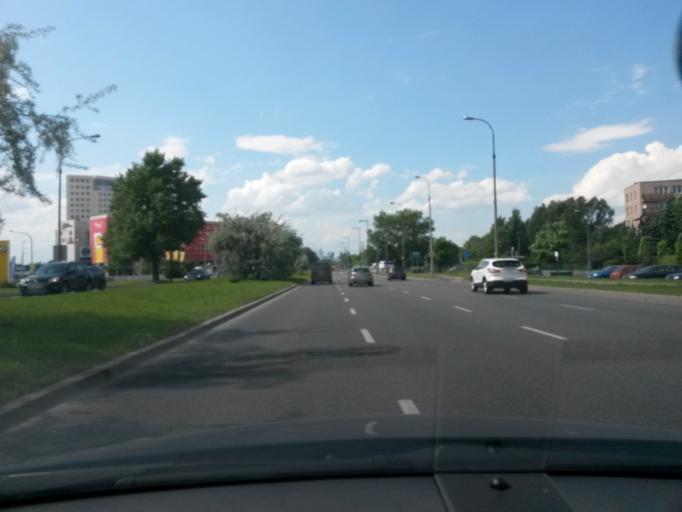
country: PL
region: Masovian Voivodeship
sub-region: Warszawa
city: Mokotow
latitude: 52.1884
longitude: 21.0489
